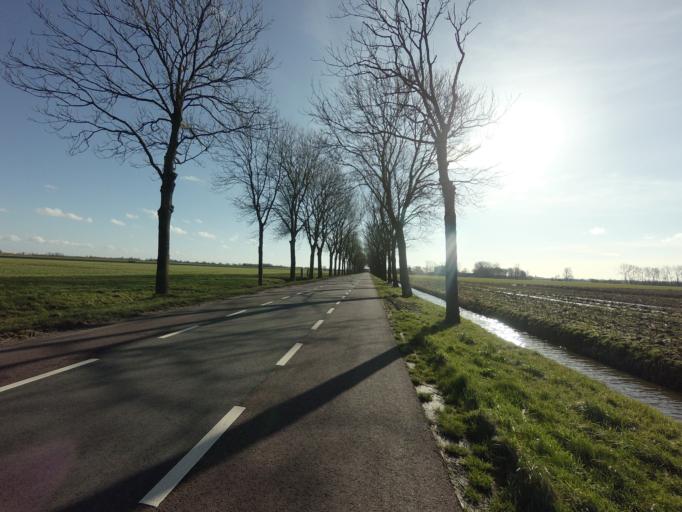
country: NL
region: Utrecht
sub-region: Gemeente Montfoort
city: Montfoort
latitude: 52.0699
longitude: 4.9606
